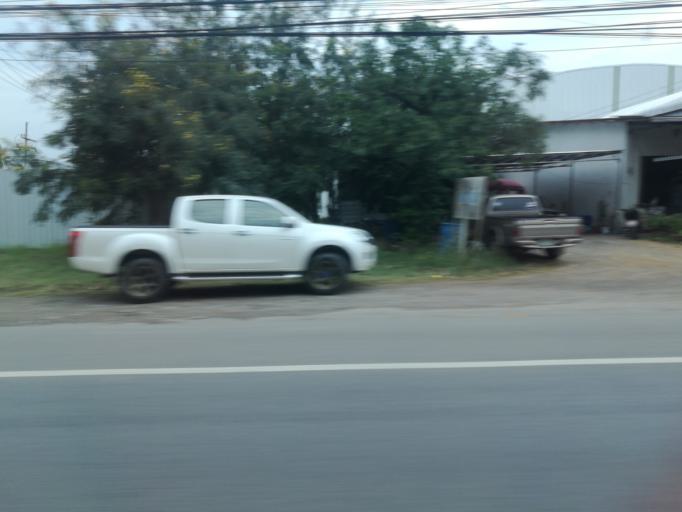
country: TH
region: Prachuap Khiri Khan
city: Pran Buri
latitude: 12.3469
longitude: 99.8827
